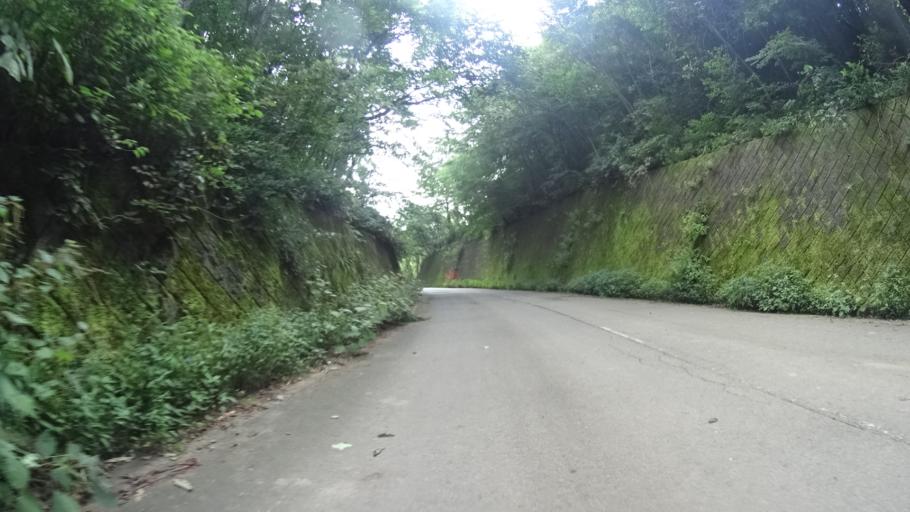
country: JP
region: Yamanashi
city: Nirasaki
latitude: 35.9058
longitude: 138.4666
